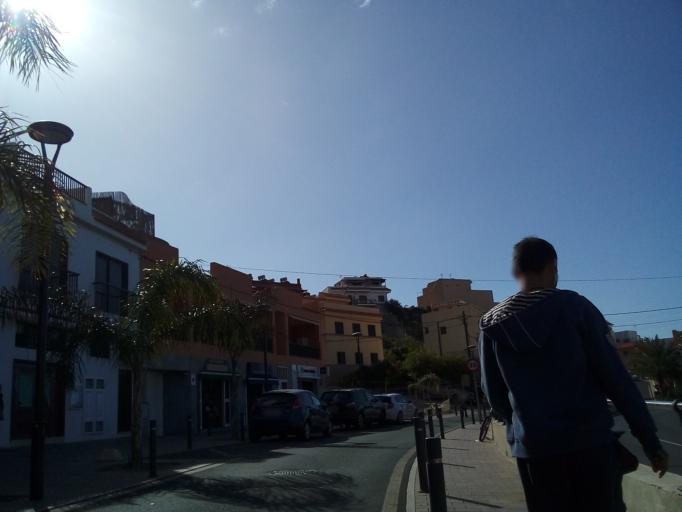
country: ES
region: Canary Islands
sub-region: Provincia de Santa Cruz de Tenerife
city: Alajero
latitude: 28.0852
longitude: -17.3344
